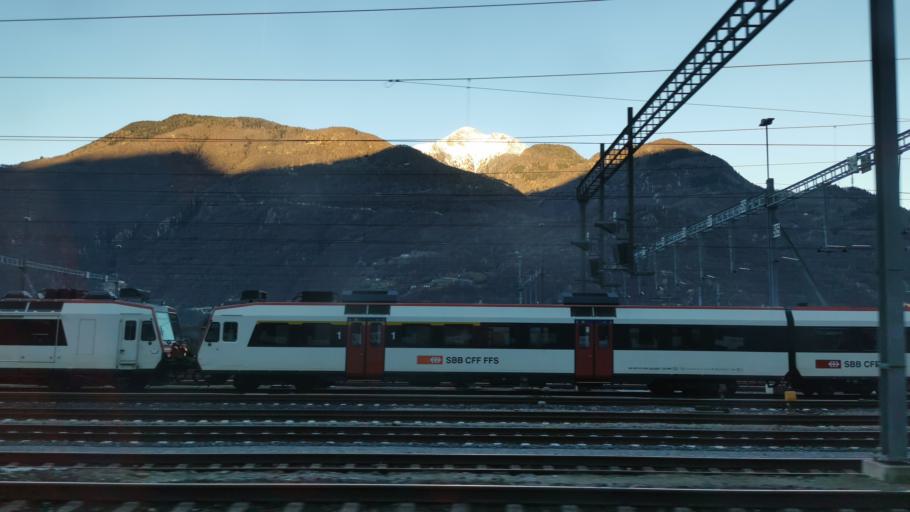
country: CH
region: Ticino
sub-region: Bellinzona District
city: Bellinzona
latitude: 46.2044
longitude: 9.0390
